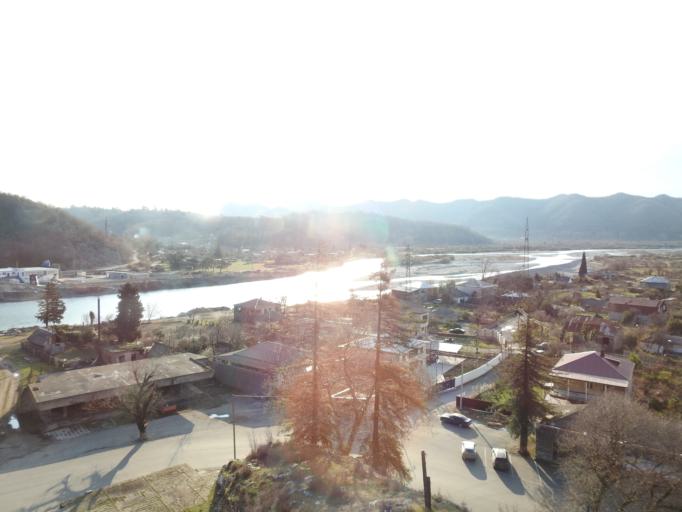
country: GE
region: Abkhazia
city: Bich'vinta
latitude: 43.2401
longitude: 40.3965
